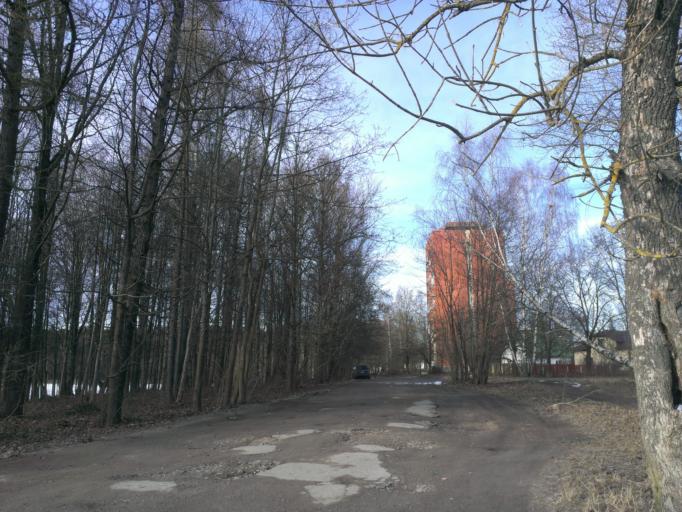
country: LV
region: Riga
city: Bergi
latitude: 56.9750
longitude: 24.2421
